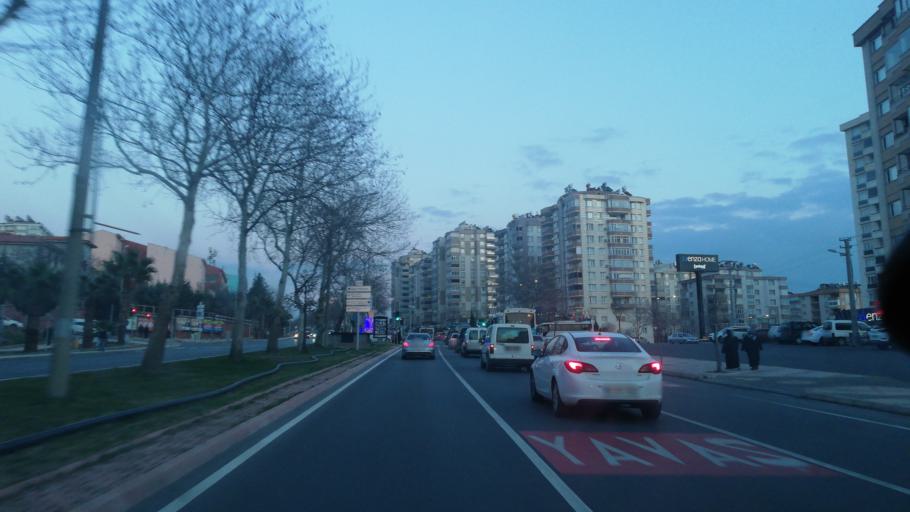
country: TR
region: Kahramanmaras
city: Kahramanmaras
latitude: 37.5893
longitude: 36.8768
